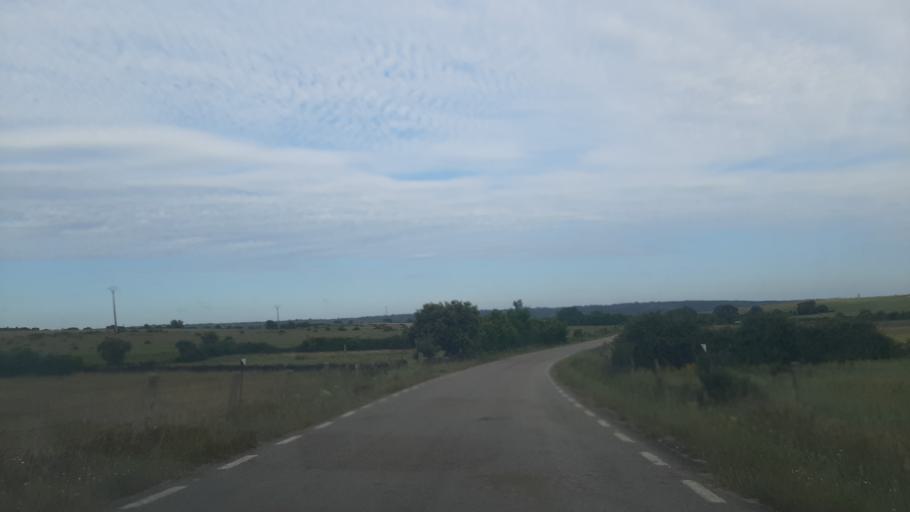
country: ES
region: Castille and Leon
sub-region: Provincia de Salamanca
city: Gallegos de Arganan
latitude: 40.6440
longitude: -6.7439
